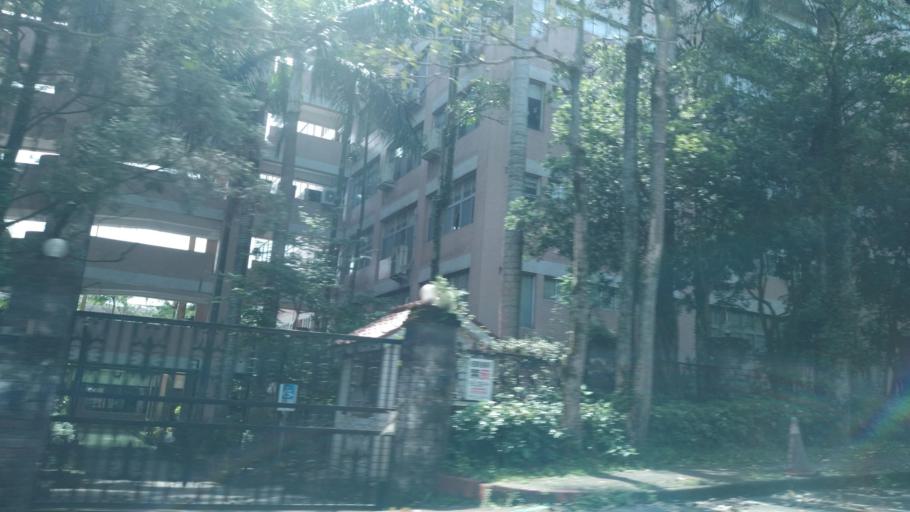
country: TW
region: Taipei
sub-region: Taipei
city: Banqiao
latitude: 24.9520
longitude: 121.5088
